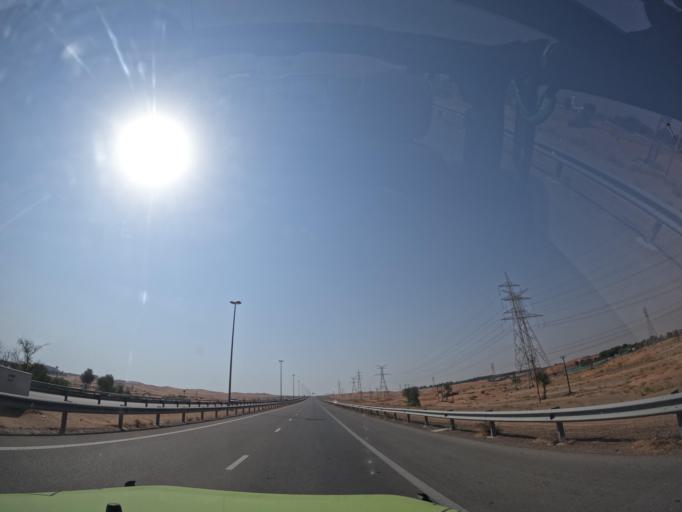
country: OM
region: Al Buraimi
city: Al Buraymi
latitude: 24.3571
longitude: 55.7335
